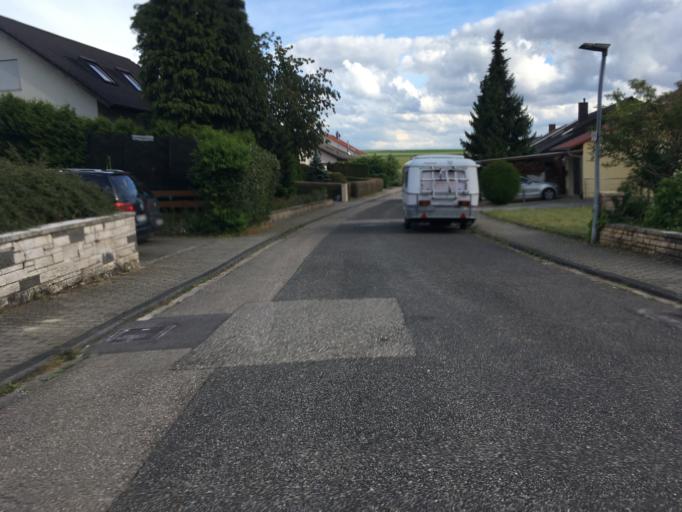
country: DE
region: Baden-Wuerttemberg
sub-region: Regierungsbezirk Stuttgart
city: Bad Rappenau
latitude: 49.2507
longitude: 9.1295
